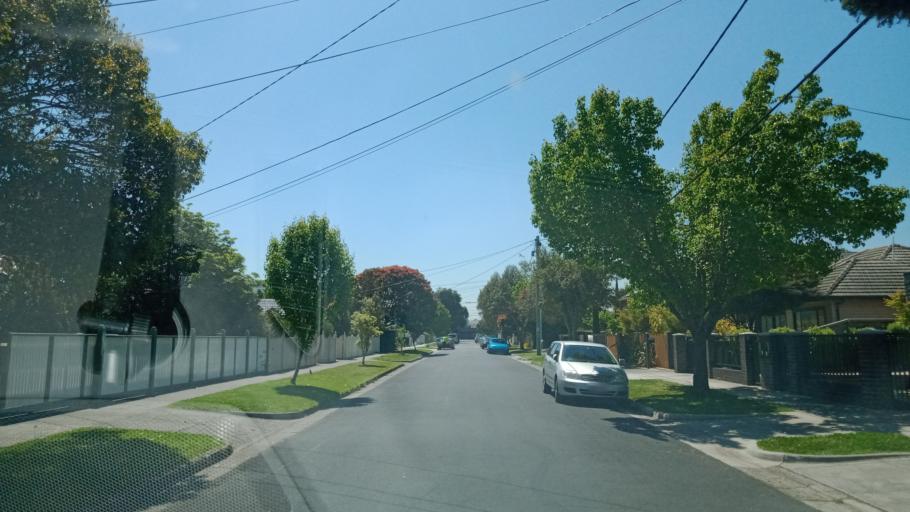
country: AU
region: Victoria
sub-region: Monash
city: Oakleigh South
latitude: -37.9253
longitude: 145.0780
